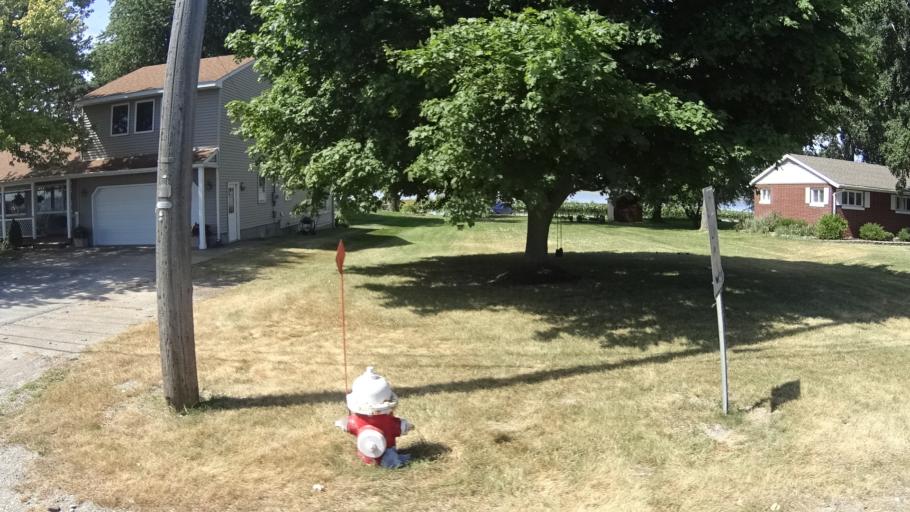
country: US
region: Ohio
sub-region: Erie County
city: Huron
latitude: 41.4342
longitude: -82.6225
